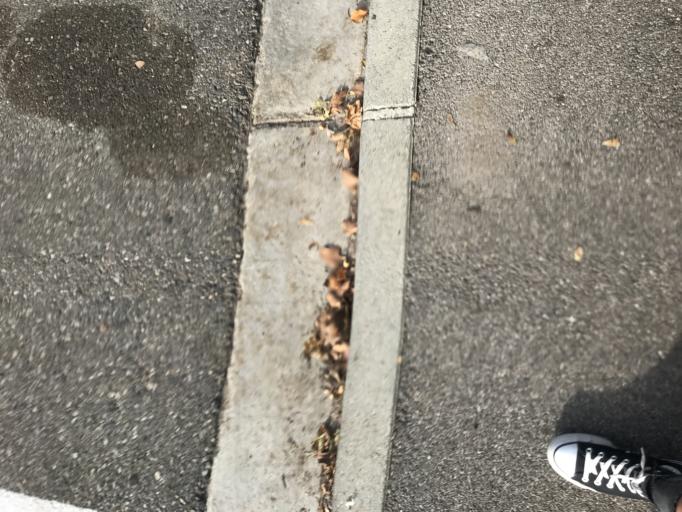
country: FR
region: Provence-Alpes-Cote d'Azur
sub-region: Departement des Bouches-du-Rhone
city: Aix-en-Provence
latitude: 43.5257
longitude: 5.4324
